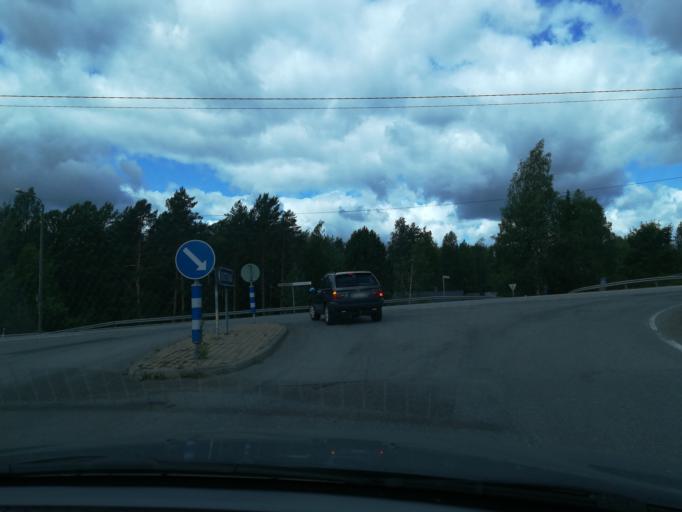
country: FI
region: Southern Savonia
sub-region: Mikkeli
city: Ristiina
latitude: 61.5133
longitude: 27.2421
